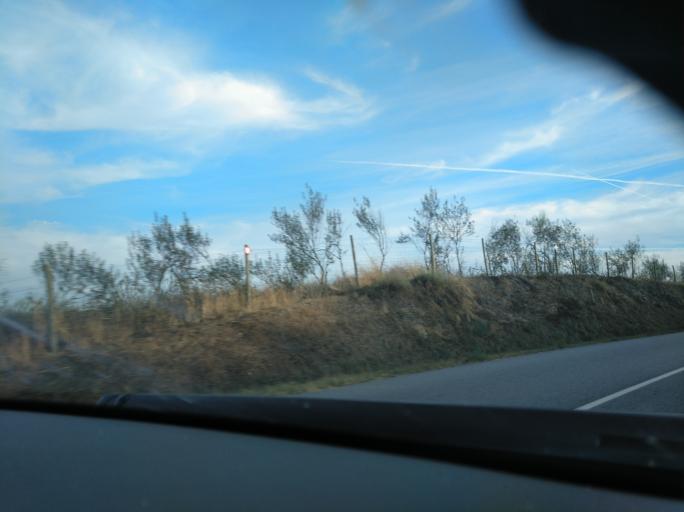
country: PT
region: Portalegre
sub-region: Avis
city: Avis
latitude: 38.8675
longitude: -7.8231
